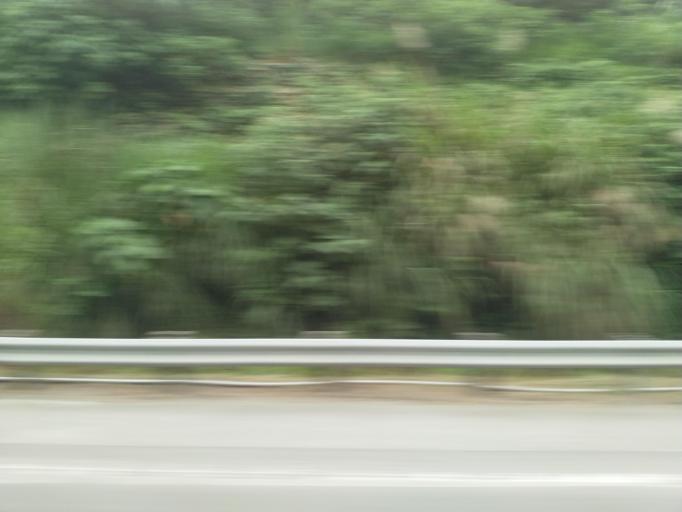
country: TW
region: Taiwan
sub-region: Pingtung
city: Pingtung
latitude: 22.7900
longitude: 120.4294
